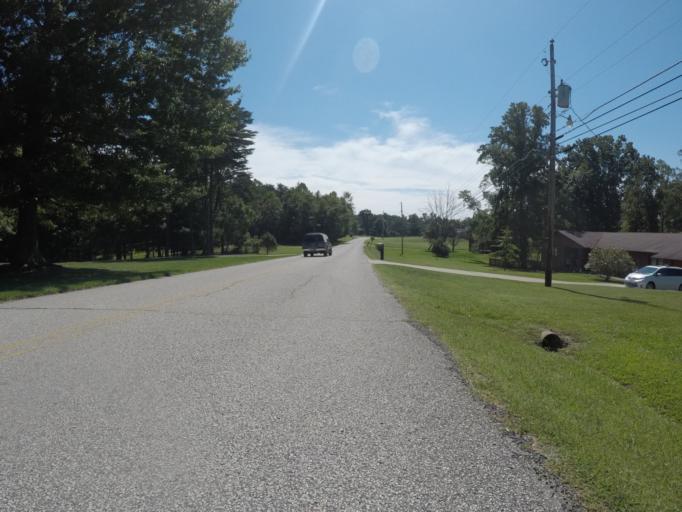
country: US
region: Kentucky
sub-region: Boyd County
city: Meads
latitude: 38.4154
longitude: -82.6601
